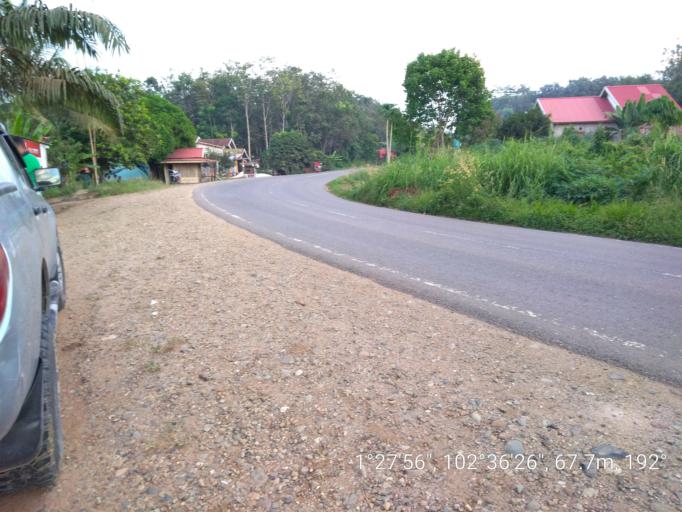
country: ID
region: Jambi
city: Sungaibengkal
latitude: -1.4657
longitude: 102.6073
